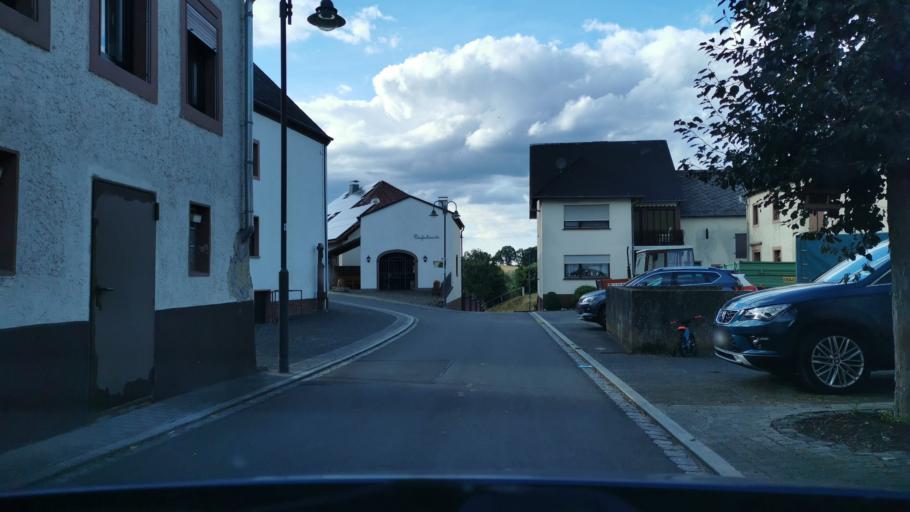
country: DE
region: Rheinland-Pfalz
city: Niersbach
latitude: 49.9311
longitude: 6.7480
